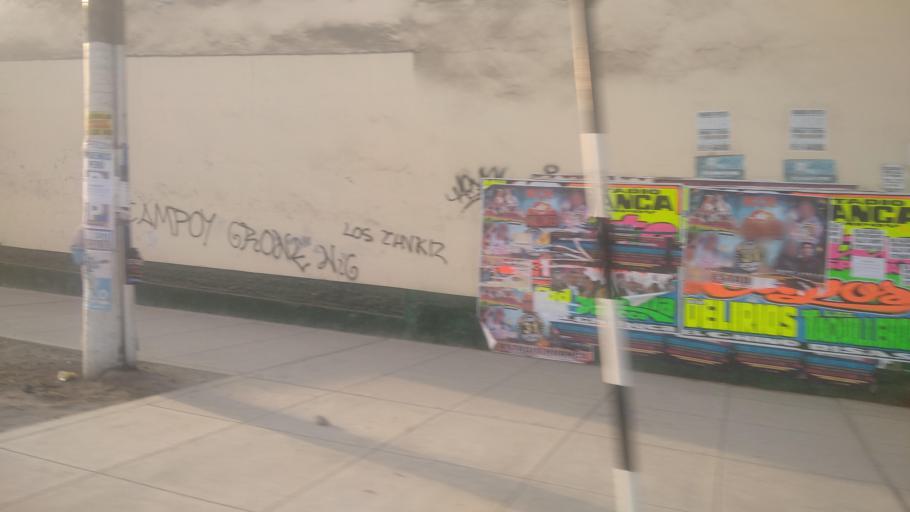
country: PE
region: Lima
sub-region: Lima
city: Vitarte
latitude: -12.0222
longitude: -76.9629
